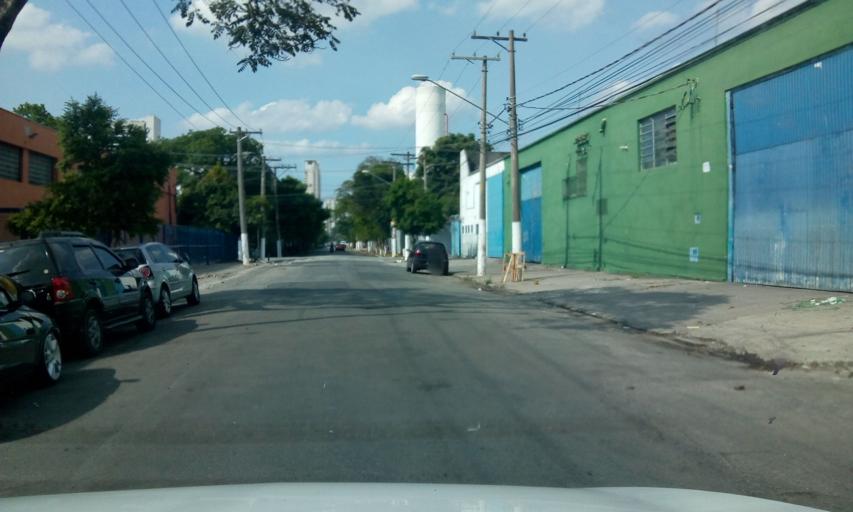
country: BR
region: Sao Paulo
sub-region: Osasco
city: Osasco
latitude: -23.5334
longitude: -46.7419
